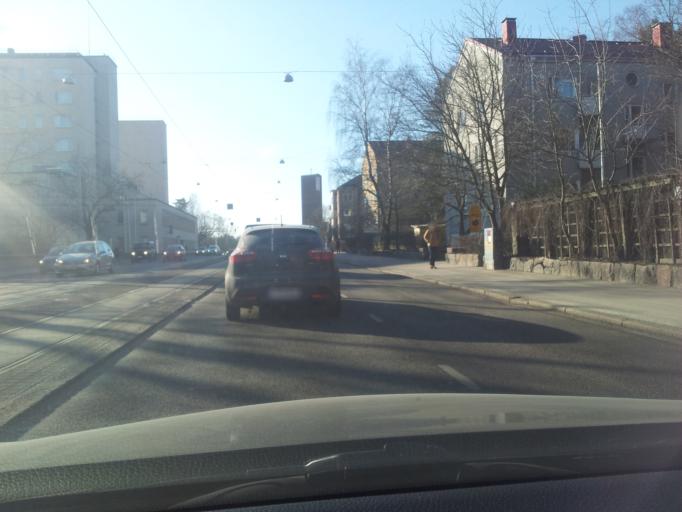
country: FI
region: Uusimaa
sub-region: Helsinki
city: Helsinki
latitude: 60.1914
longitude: 24.9042
